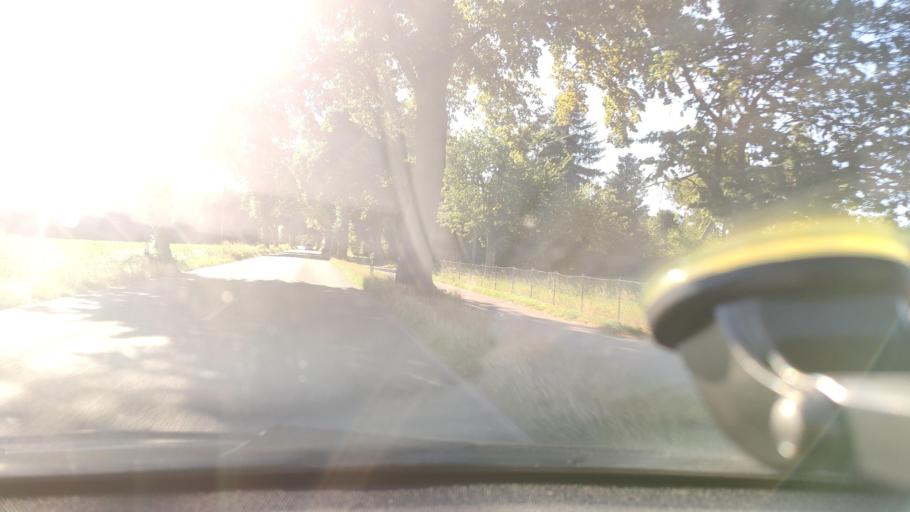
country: DE
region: North Rhine-Westphalia
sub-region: Regierungsbezirk Dusseldorf
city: Goch
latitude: 51.6790
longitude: 6.0955
